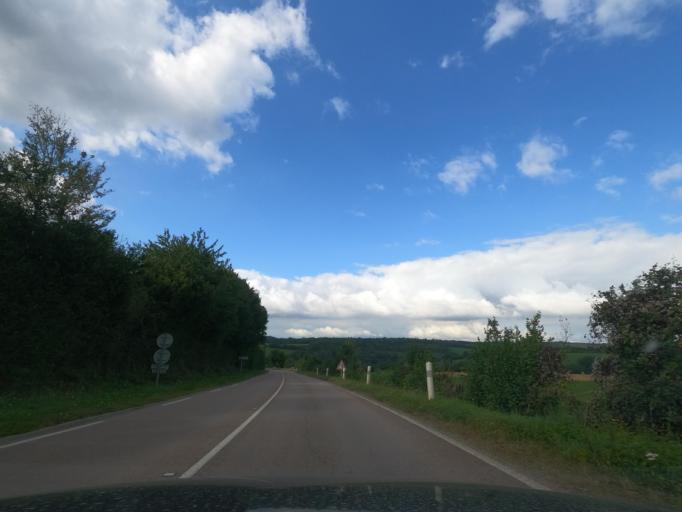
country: FR
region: Lower Normandy
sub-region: Departement de l'Orne
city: Gace
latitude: 48.8035
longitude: 0.3110
